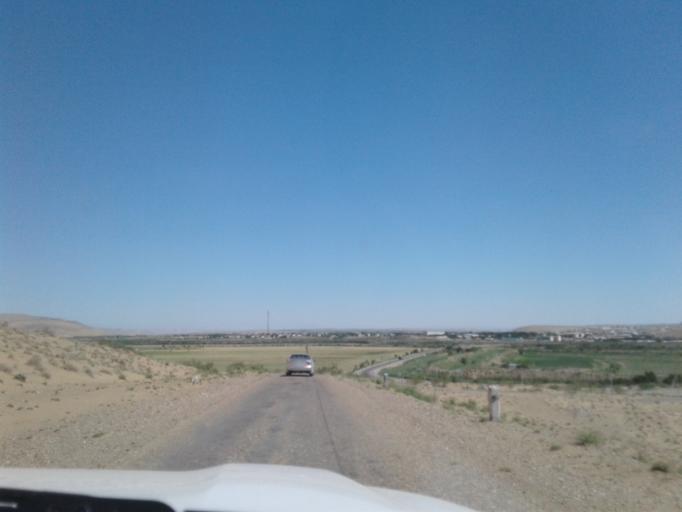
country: AF
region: Badghis
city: Bala Murghab
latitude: 35.9755
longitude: 62.9015
